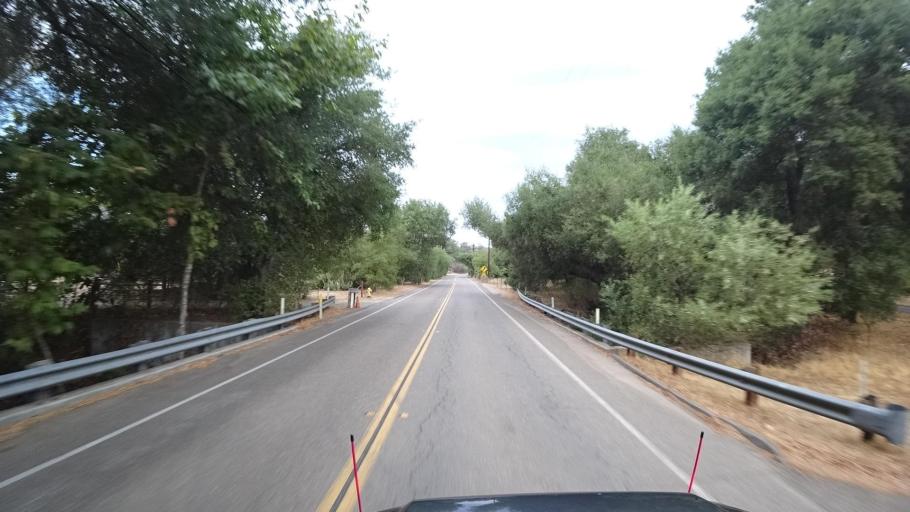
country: US
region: California
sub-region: San Diego County
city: Ramona
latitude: 32.9716
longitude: -116.9156
